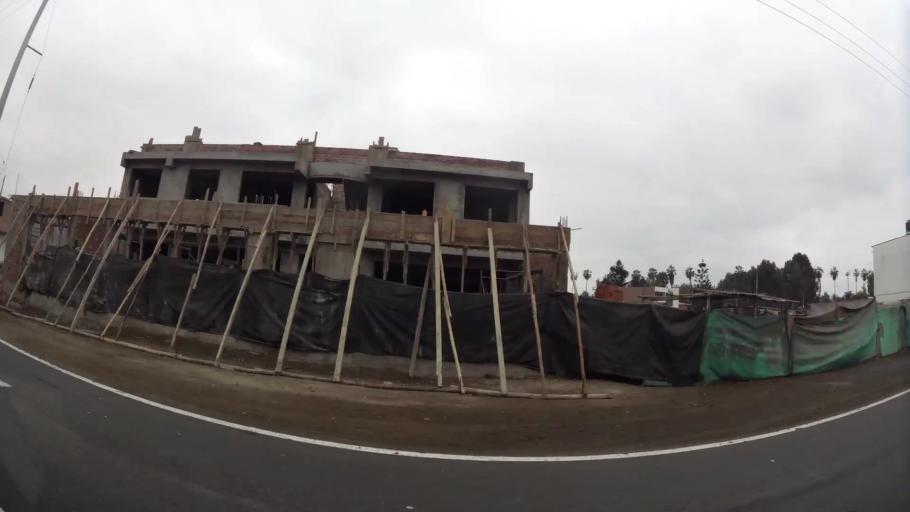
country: PE
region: Lima
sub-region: Lima
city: Surco
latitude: -12.2056
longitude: -77.0100
